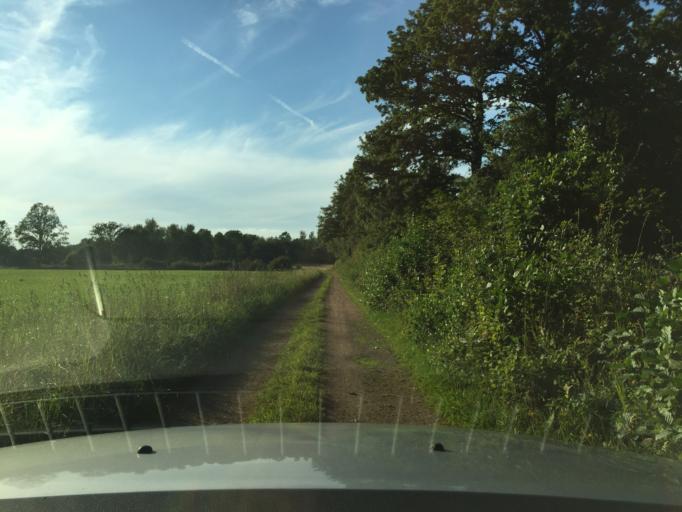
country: SE
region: Skane
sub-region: Hassleholms Kommun
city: Sosdala
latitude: 56.0244
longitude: 13.7075
